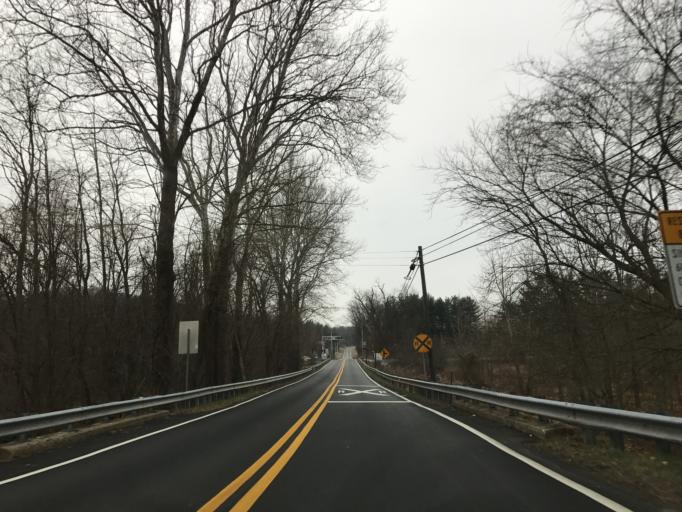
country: US
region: Maryland
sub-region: Carroll County
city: Westminster
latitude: 39.5581
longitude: -77.0332
